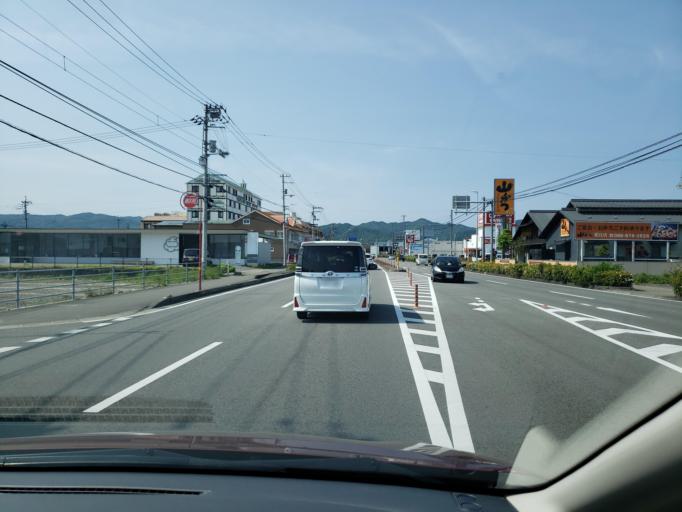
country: JP
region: Tokushima
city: Ishii
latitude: 34.1244
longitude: 134.4773
